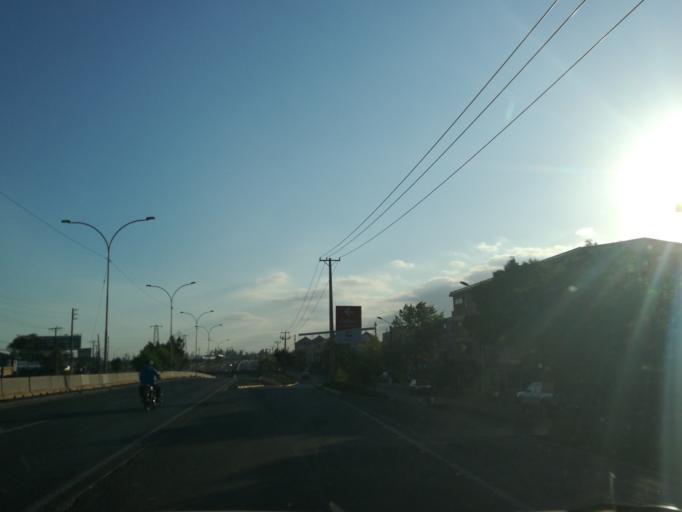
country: CL
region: O'Higgins
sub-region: Provincia de Cachapoal
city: Rancagua
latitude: -34.1824
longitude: -70.7379
